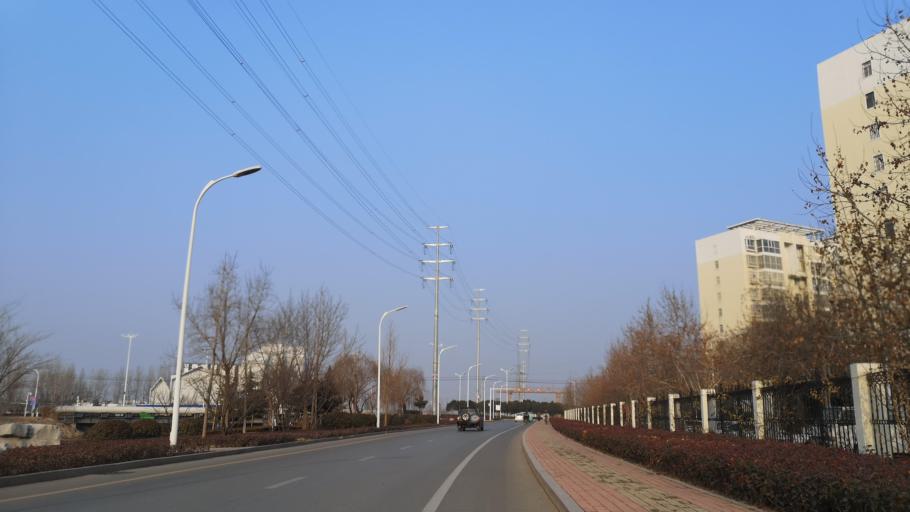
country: CN
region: Henan Sheng
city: Zhongyuanlu
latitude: 35.7892
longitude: 115.0598
